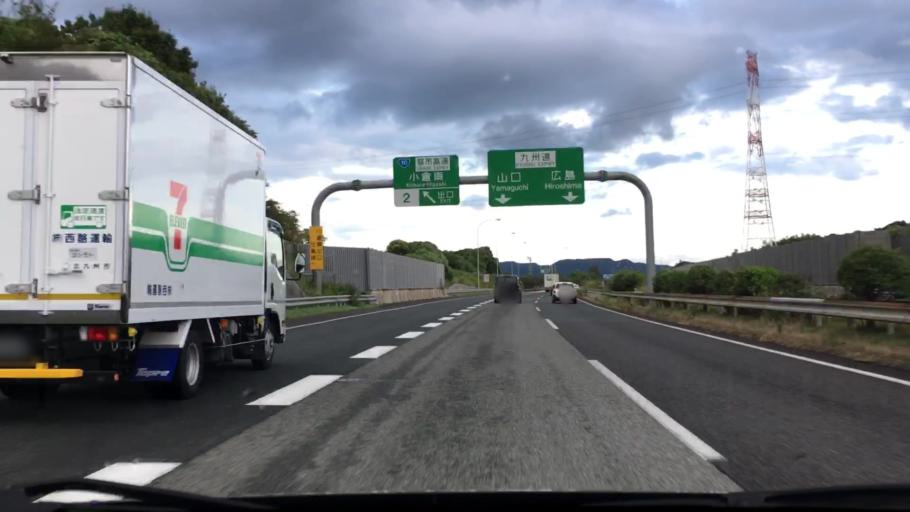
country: JP
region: Fukuoka
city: Kitakyushu
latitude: 33.8322
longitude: 130.9065
